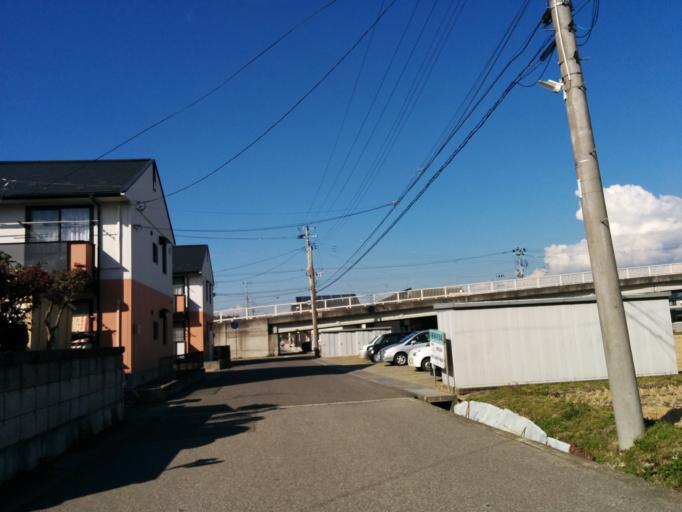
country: JP
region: Fukushima
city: Kitakata
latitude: 37.4783
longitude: 139.9125
